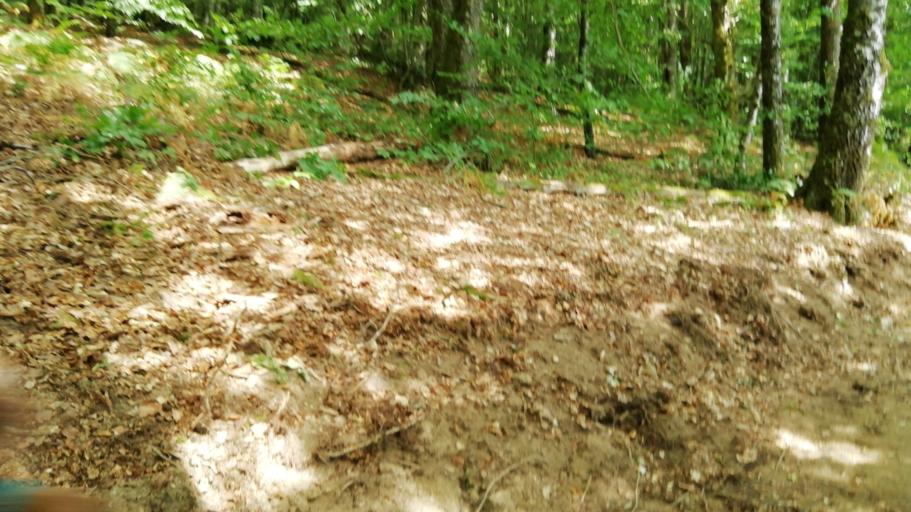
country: FR
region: Auvergne
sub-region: Departement du Cantal
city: Laroquebrou
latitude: 44.9453
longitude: 2.2302
